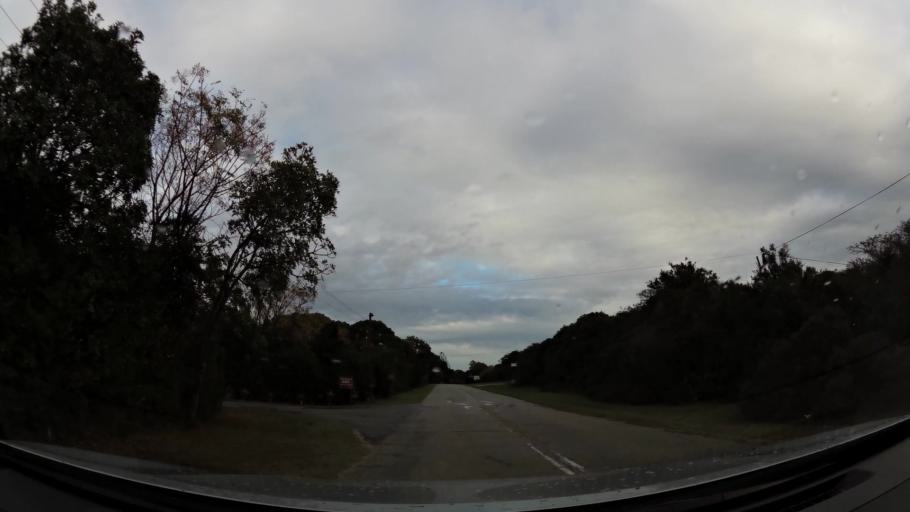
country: ZA
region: Eastern Cape
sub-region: Nelson Mandela Bay Metropolitan Municipality
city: Port Elizabeth
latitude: -34.0160
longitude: 25.5074
